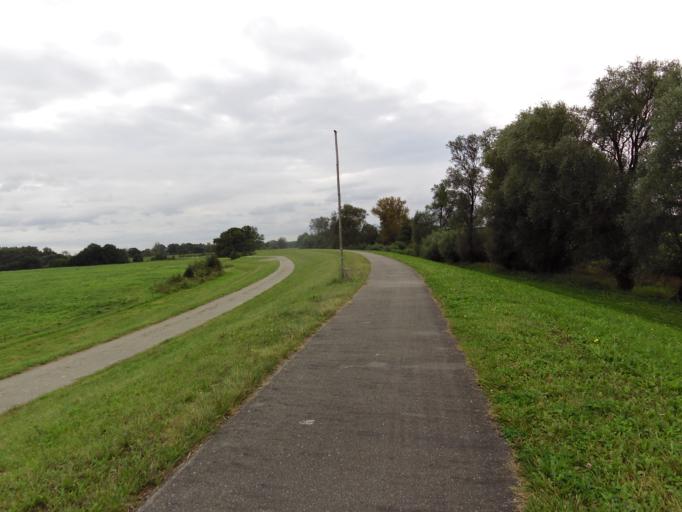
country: DE
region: Brandenburg
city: Ruhstadt
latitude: 52.9204
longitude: 11.8408
